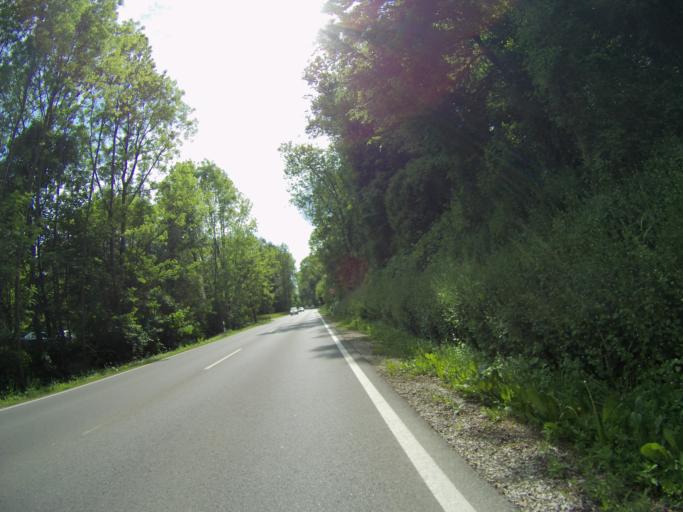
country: DE
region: Bavaria
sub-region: Upper Bavaria
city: Marzling
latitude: 48.4089
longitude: 11.7717
